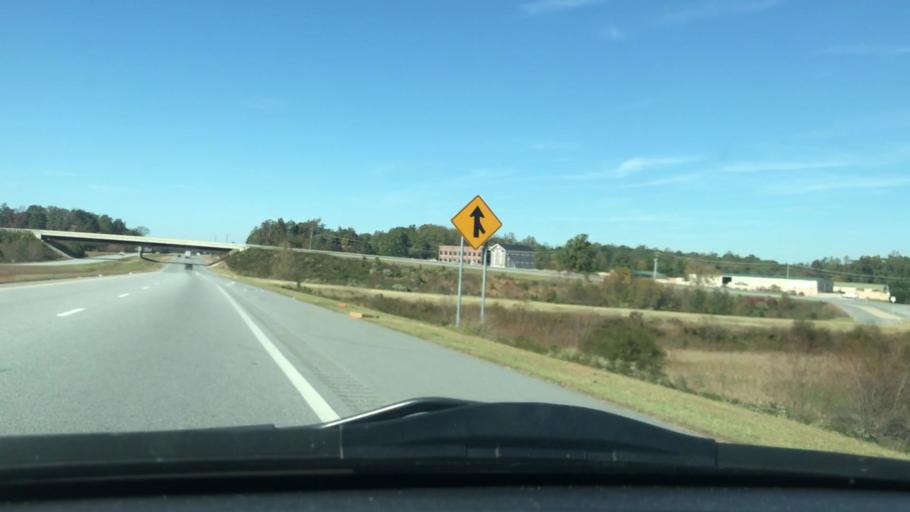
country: US
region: North Carolina
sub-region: Randolph County
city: Archdale
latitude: 35.8724
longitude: -79.8997
